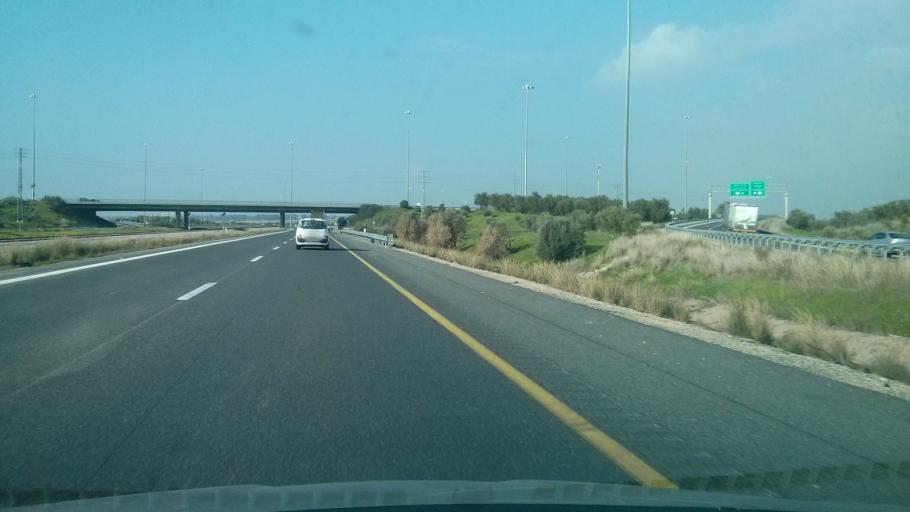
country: IL
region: Central District
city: Gedera
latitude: 31.7914
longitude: 34.8317
